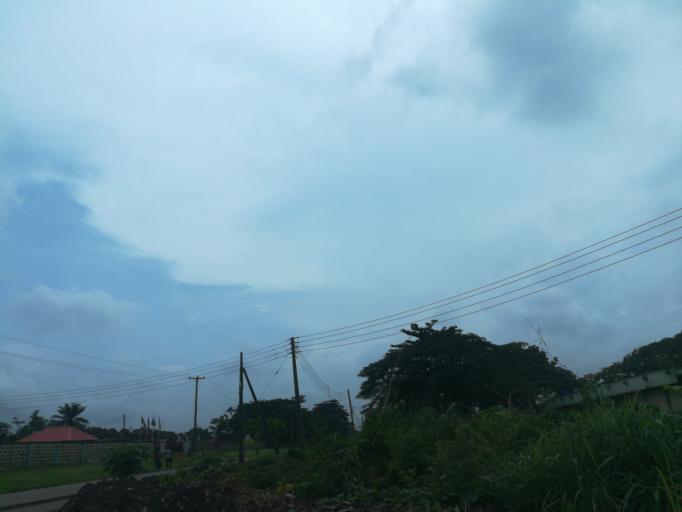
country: NG
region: Lagos
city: Oshodi
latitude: 6.5674
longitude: 3.3576
